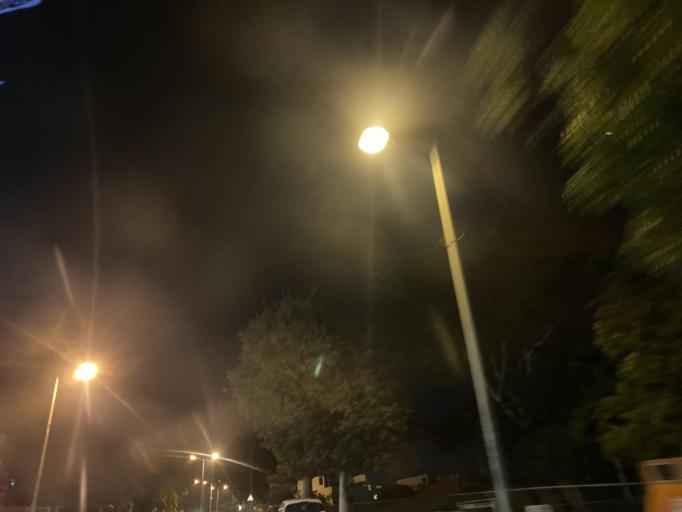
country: IL
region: Haifa
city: Daliyat el Karmil
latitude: 32.6404
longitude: 35.0837
